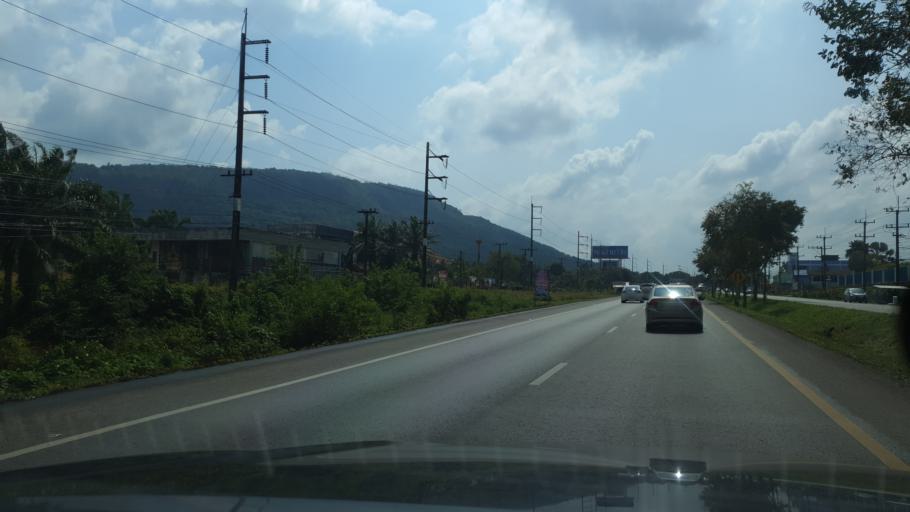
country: TH
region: Chumphon
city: Tha Sae
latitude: 10.5842
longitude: 99.1139
